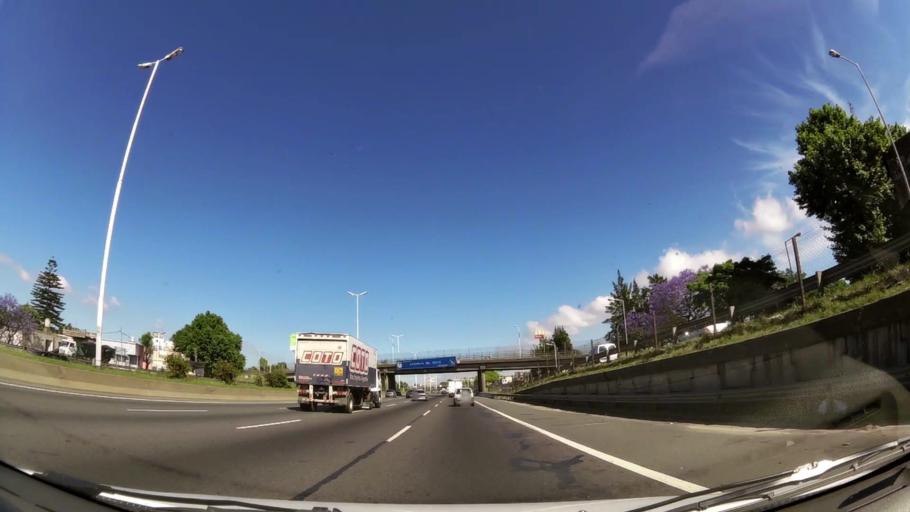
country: AR
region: Buenos Aires
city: Caseros
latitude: -34.6319
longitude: -58.5445
